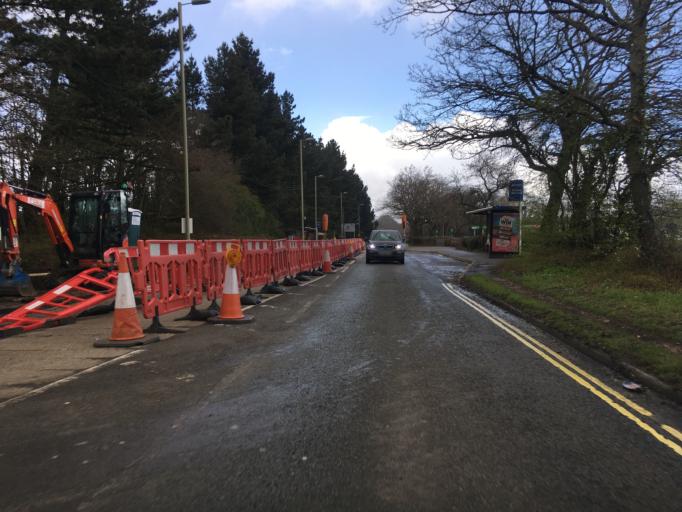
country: GB
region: England
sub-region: Hampshire
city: Eastleigh
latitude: 50.9674
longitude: -1.3914
